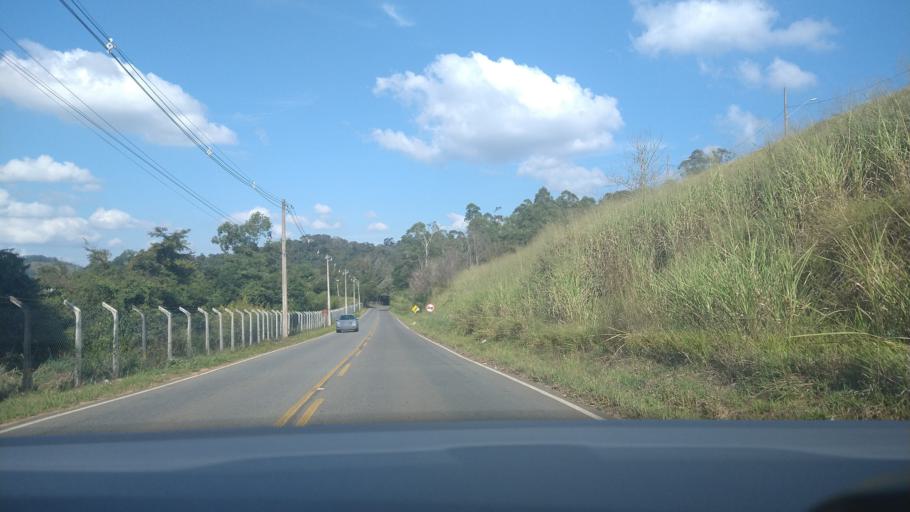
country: BR
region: Minas Gerais
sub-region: Vicosa
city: Vicosa
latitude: -20.7618
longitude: -42.8727
